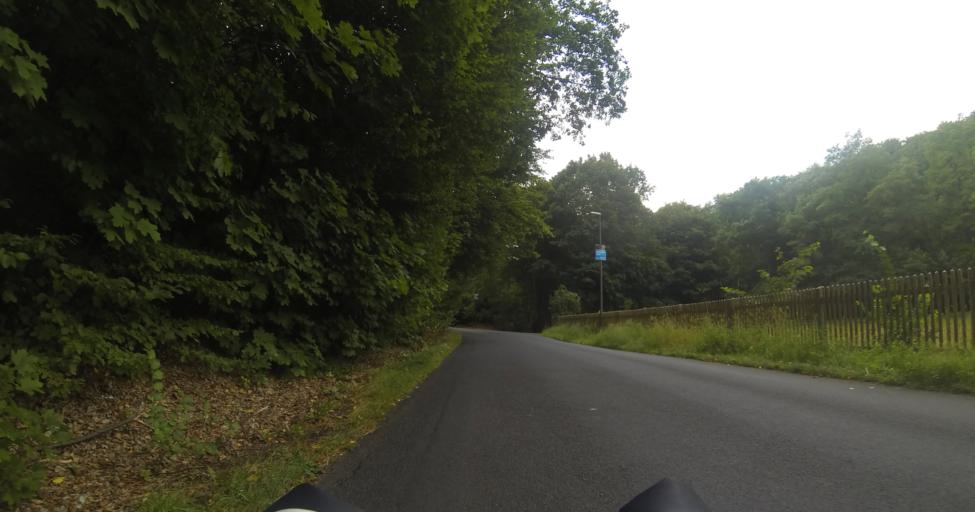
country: DE
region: Saxony
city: Radebeul
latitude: 51.1194
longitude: 13.6551
